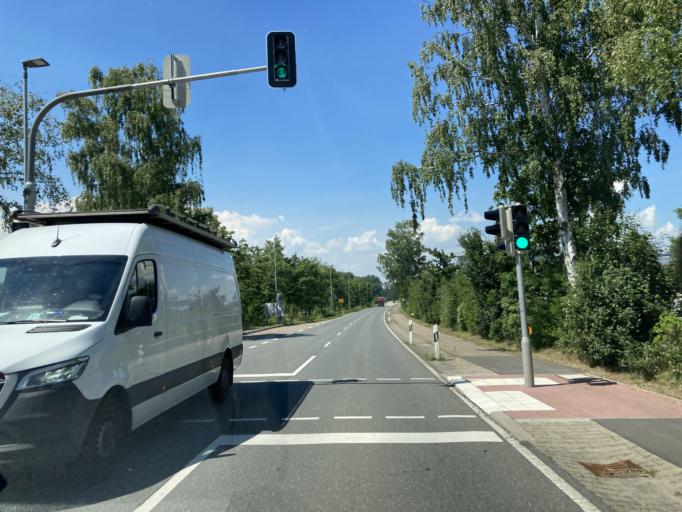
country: DE
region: Baden-Wuerttemberg
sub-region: Karlsruhe Region
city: Graben-Neudorf
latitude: 49.1785
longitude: 8.4912
